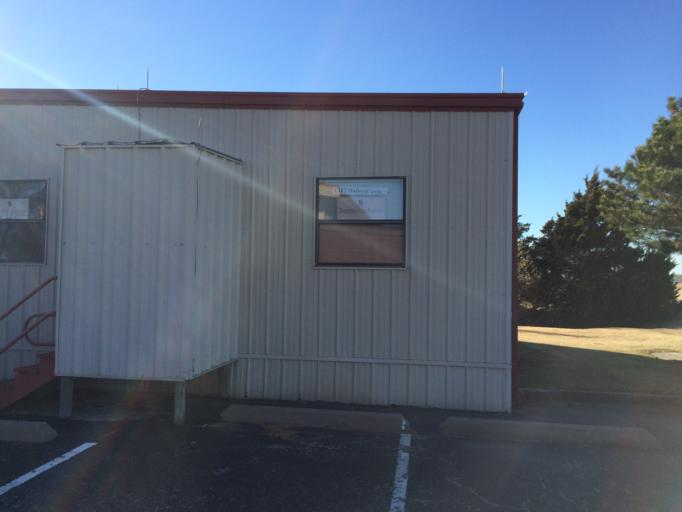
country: US
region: Oklahoma
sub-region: Cleveland County
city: Norman
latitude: 35.2377
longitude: -97.4626
